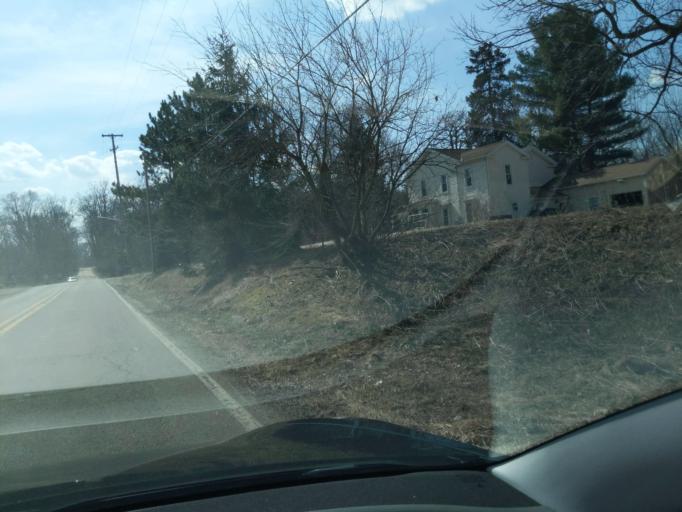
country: US
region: Michigan
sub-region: Livingston County
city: Pinckney
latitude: 42.4301
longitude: -84.0579
